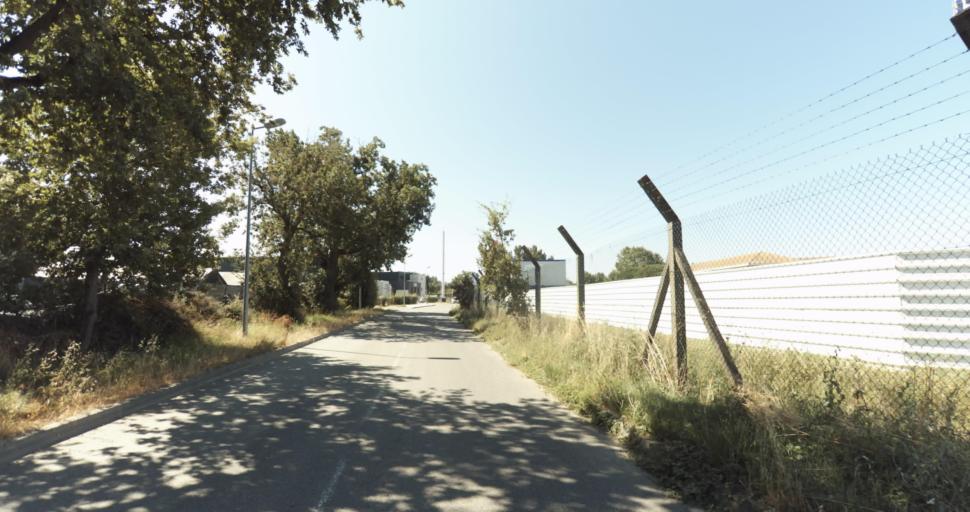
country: FR
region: Midi-Pyrenees
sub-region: Departement de la Haute-Garonne
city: L'Union
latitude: 43.6390
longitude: 1.4937
